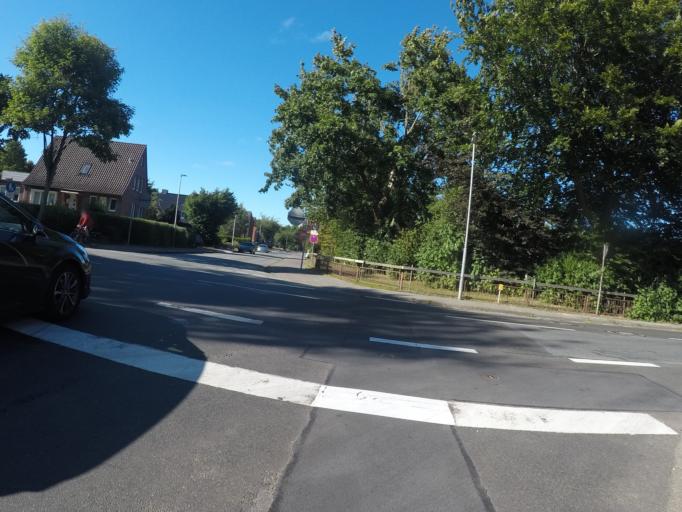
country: DE
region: Lower Saxony
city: Otterndorf
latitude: 53.8099
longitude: 8.9067
